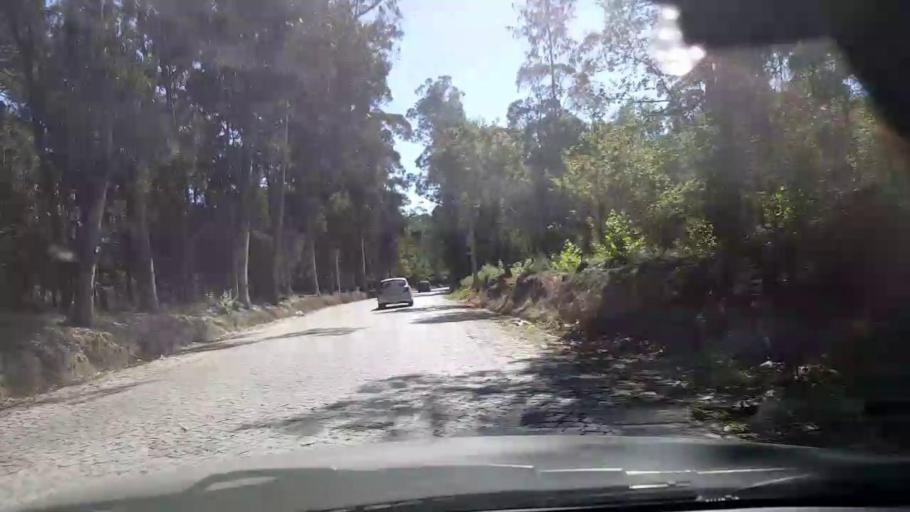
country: PT
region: Porto
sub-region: Vila do Conde
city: Arvore
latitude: 41.3244
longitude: -8.7256
